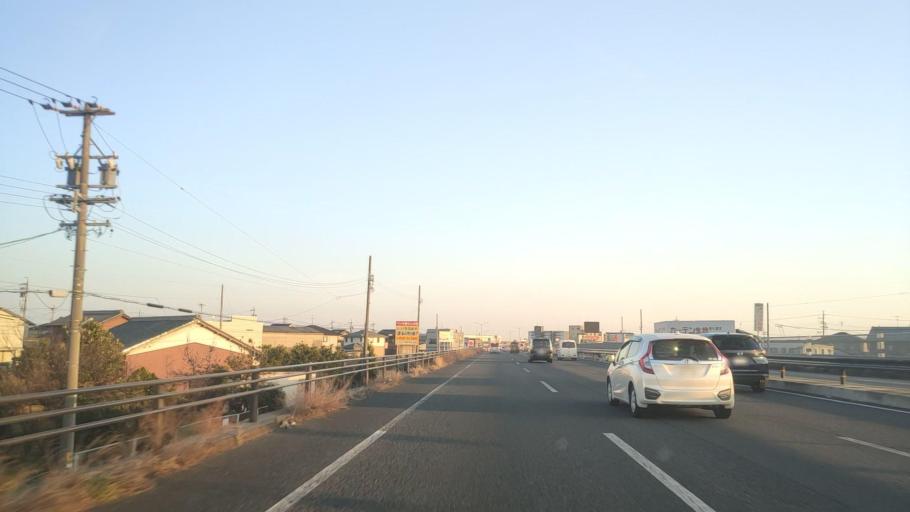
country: JP
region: Aichi
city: Kuroda
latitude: 35.3586
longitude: 136.7845
